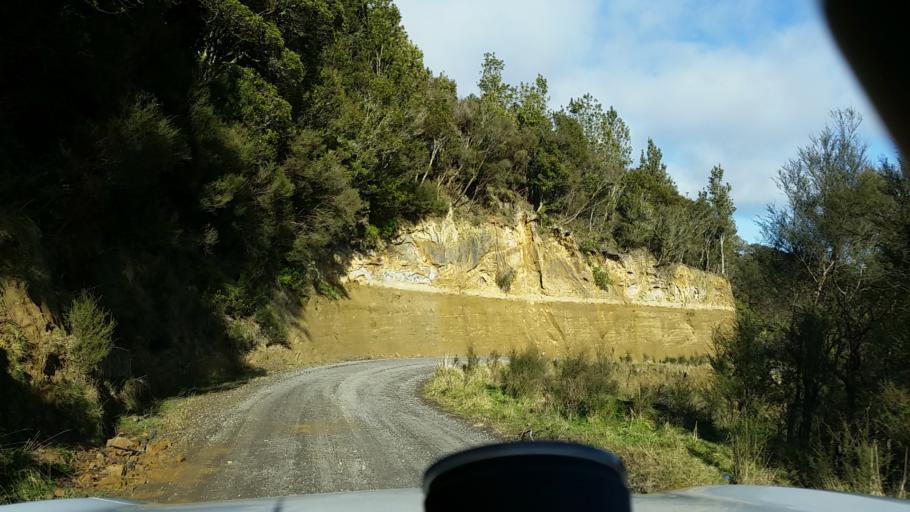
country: NZ
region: Taranaki
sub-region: South Taranaki District
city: Eltham
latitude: -39.4052
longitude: 174.5589
